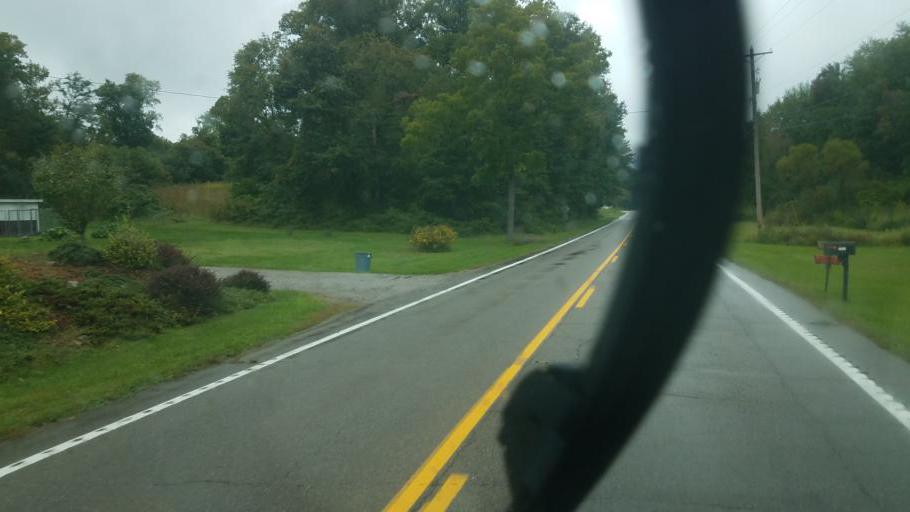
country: US
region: Ohio
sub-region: Jackson County
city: Oak Hill
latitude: 38.8597
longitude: -82.6042
